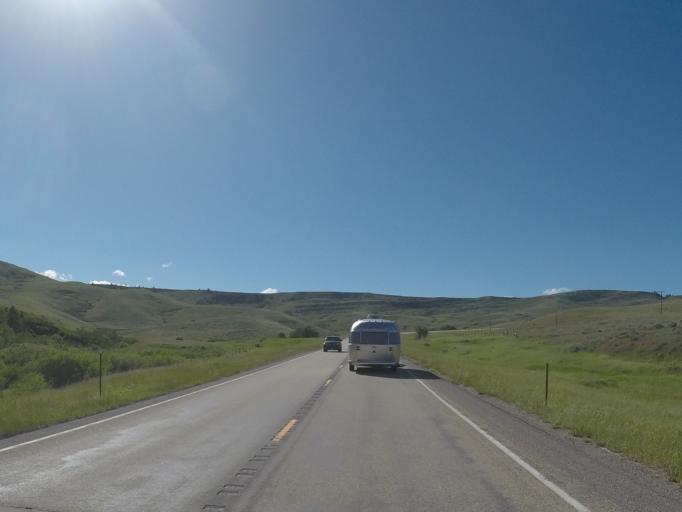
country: US
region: Montana
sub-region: Carbon County
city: Red Lodge
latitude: 45.1629
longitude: -109.2131
